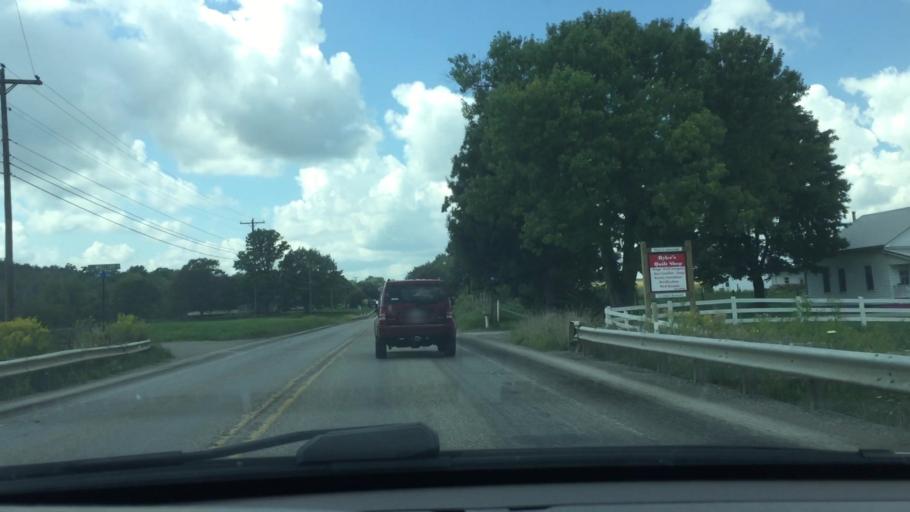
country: US
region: Pennsylvania
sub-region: Lawrence County
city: New Wilmington
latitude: 41.1181
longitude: -80.2820
